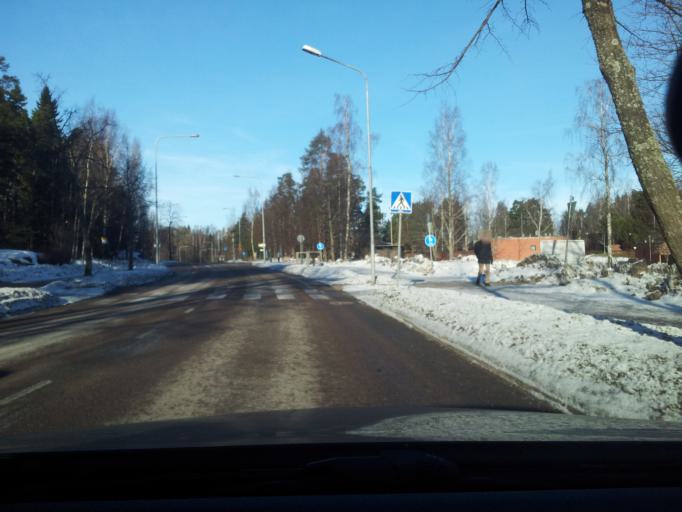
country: FI
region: Uusimaa
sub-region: Helsinki
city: Koukkuniemi
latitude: 60.1511
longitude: 24.7512
